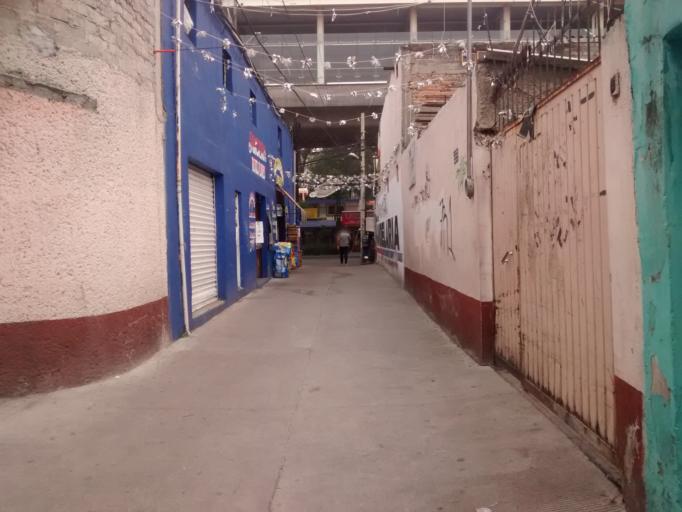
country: MX
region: Mexico City
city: Iztapalapa
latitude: 19.3276
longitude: -99.1045
